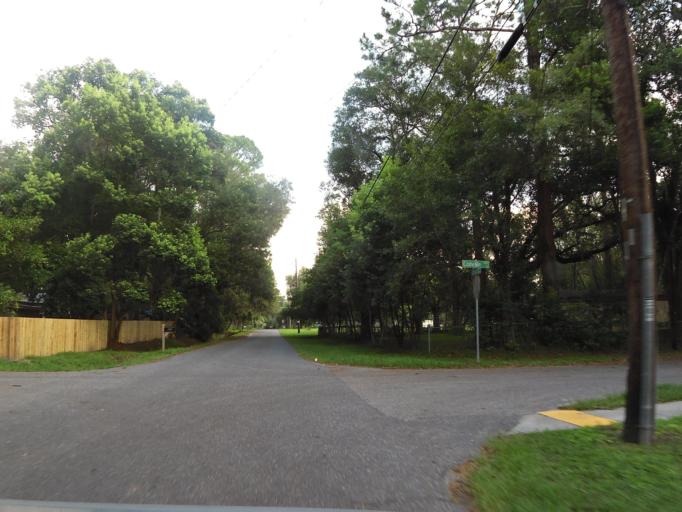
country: US
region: Florida
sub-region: Duval County
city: Jacksonville
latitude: 30.3310
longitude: -81.7860
